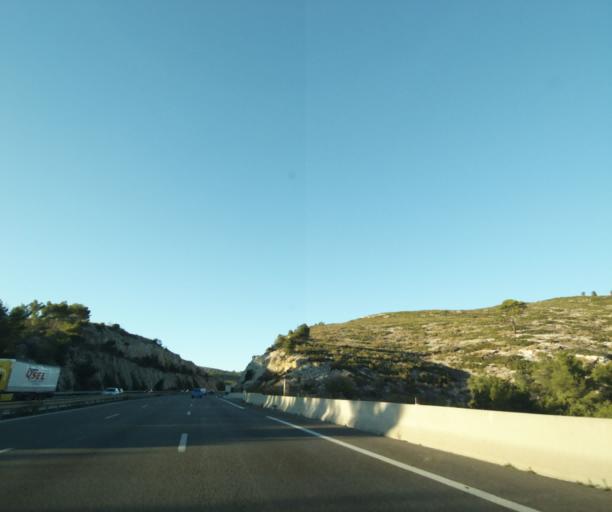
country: FR
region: Provence-Alpes-Cote d'Azur
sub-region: Departement des Bouches-du-Rhone
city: Cassis
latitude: 43.2098
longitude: 5.5841
